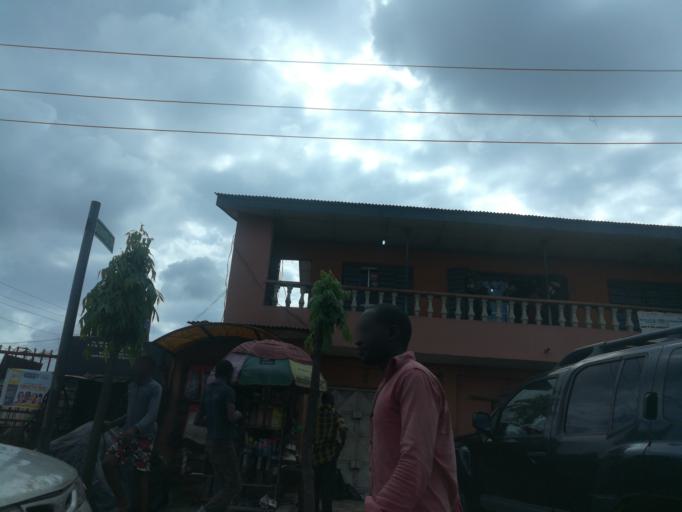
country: NG
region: Lagos
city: Agege
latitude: 6.6251
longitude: 3.3348
